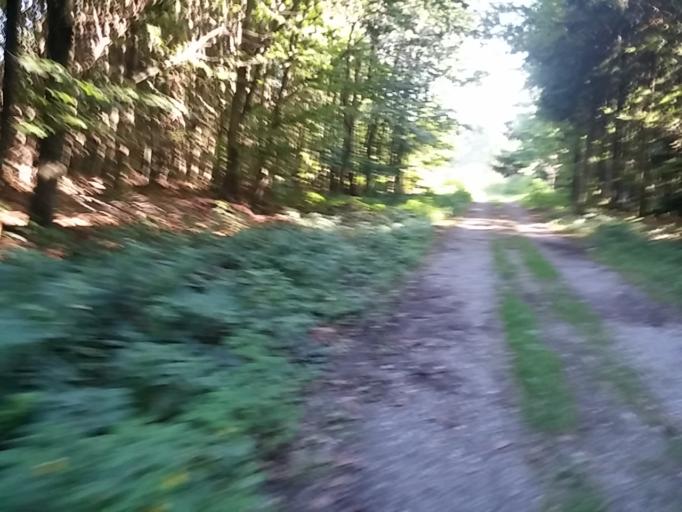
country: DE
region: Baden-Wuerttemberg
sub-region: Tuebingen Region
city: Leutkirch im Allgau
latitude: 47.7759
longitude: 10.0636
